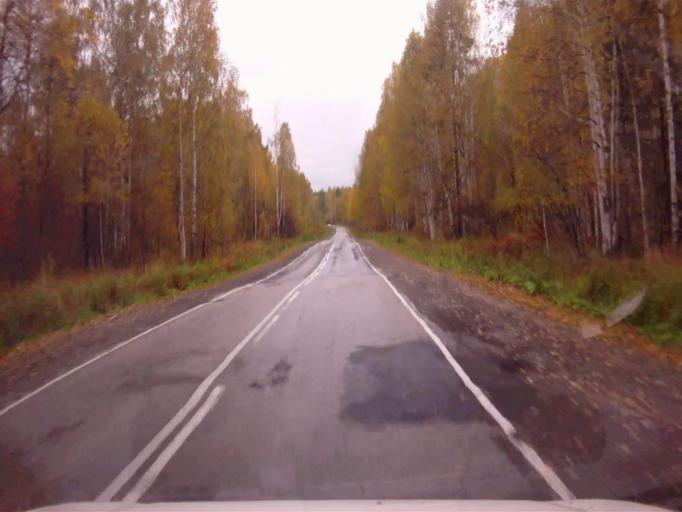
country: RU
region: Chelyabinsk
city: Nizhniy Ufaley
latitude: 56.0543
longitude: 59.9559
